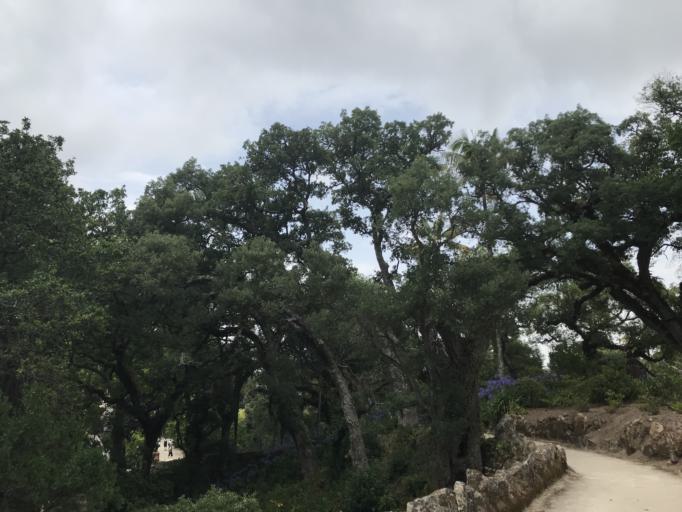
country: PT
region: Lisbon
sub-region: Sintra
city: Colares
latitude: 38.7927
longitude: -9.4199
